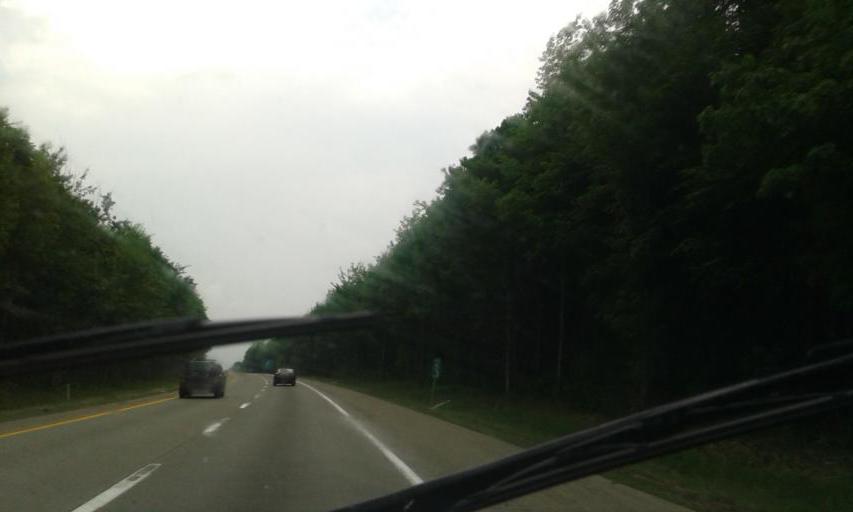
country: US
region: Pennsylvania
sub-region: Monroe County
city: Mount Pocono
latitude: 41.1445
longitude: -75.4032
